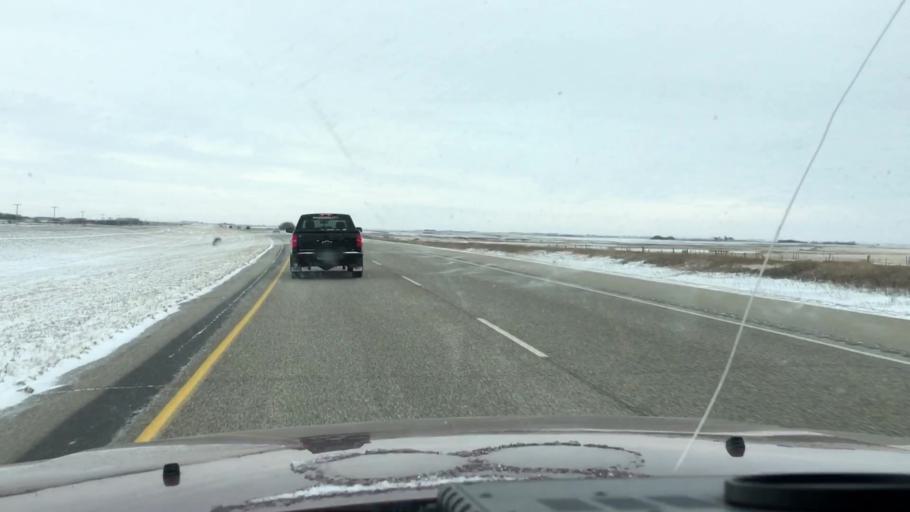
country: CA
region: Saskatchewan
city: Saskatoon
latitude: 51.6070
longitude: -106.4075
